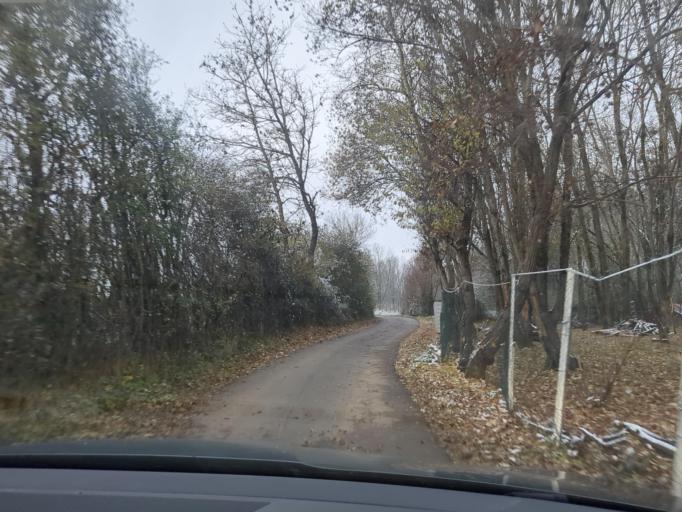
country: FR
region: Franche-Comte
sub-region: Departement du Jura
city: Perrigny
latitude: 46.6622
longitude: 5.5840
